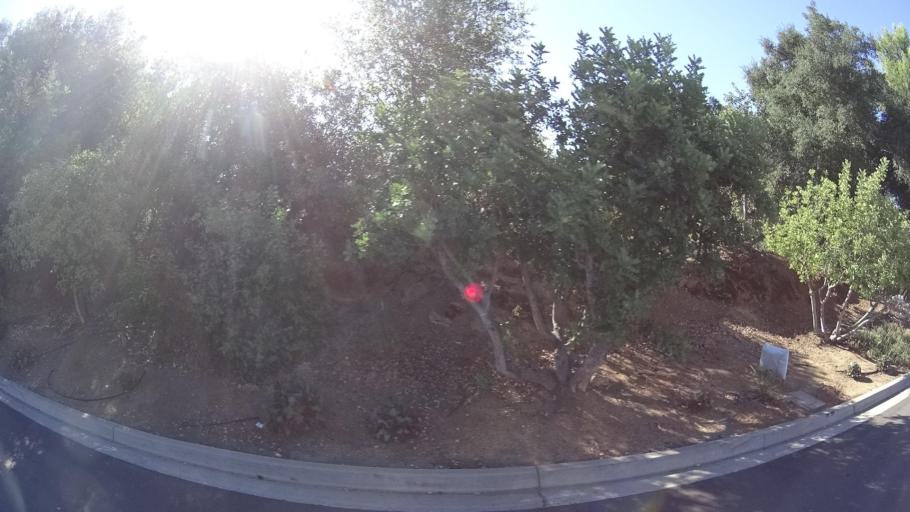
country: US
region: California
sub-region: San Diego County
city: San Diego Country Estates
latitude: 32.9976
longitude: -116.8220
